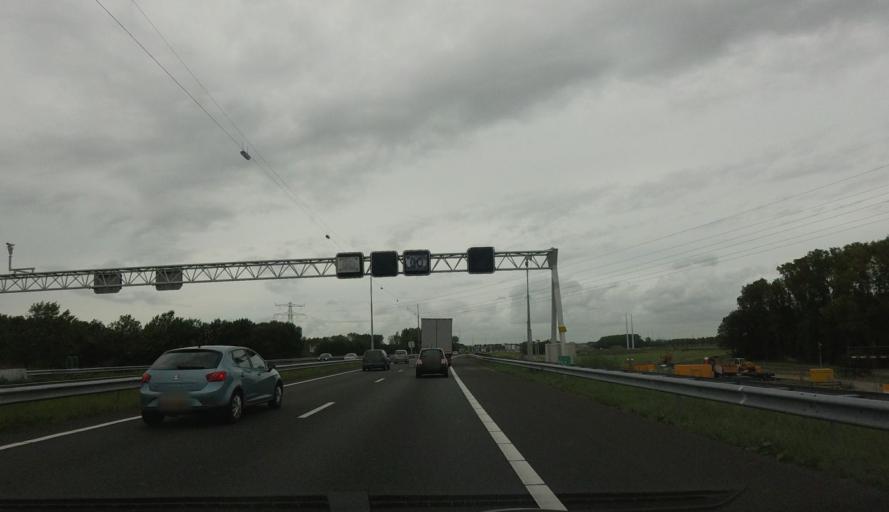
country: NL
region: North Holland
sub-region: Gemeente Velsen
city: Velsen-Zuid
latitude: 52.4451
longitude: 4.6672
